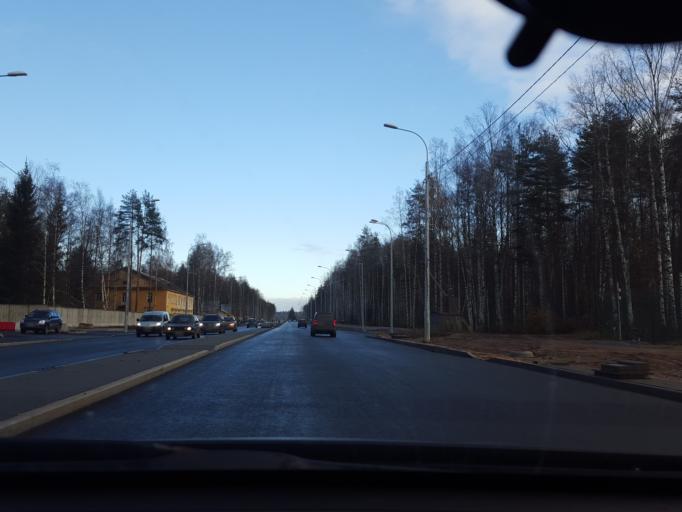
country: RU
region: St.-Petersburg
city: Pargolovo
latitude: 60.0574
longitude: 30.2405
